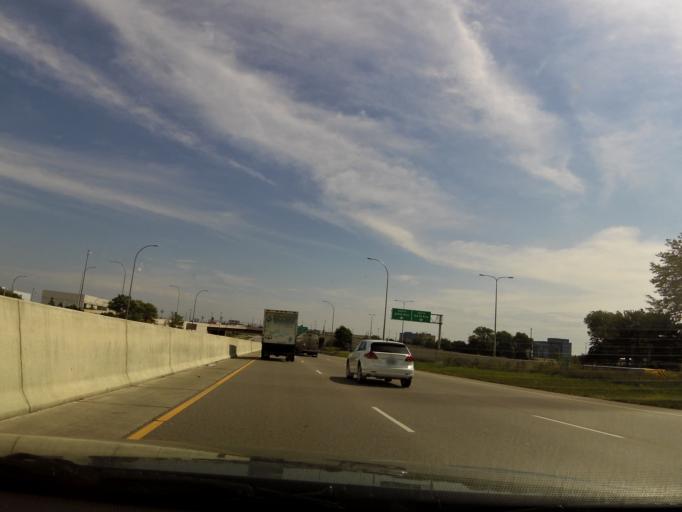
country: US
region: Minnesota
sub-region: Hennepin County
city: Richfield
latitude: 44.8622
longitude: -93.2410
